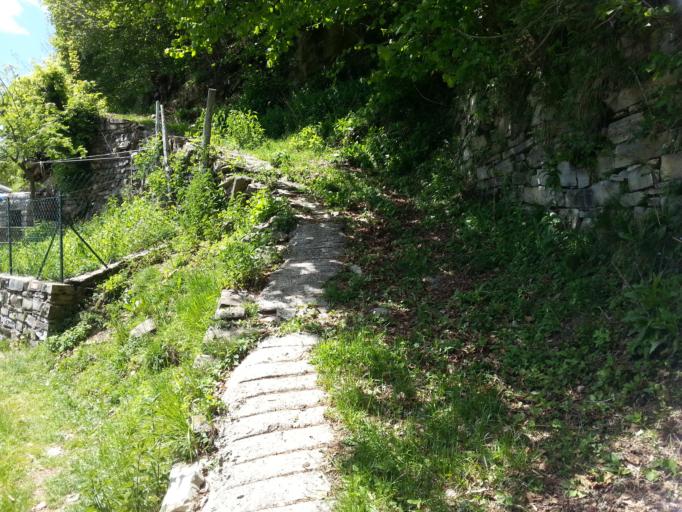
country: IT
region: Lombardy
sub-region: Provincia di Como
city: Ossuccio
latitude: 45.9993
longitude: 9.1719
